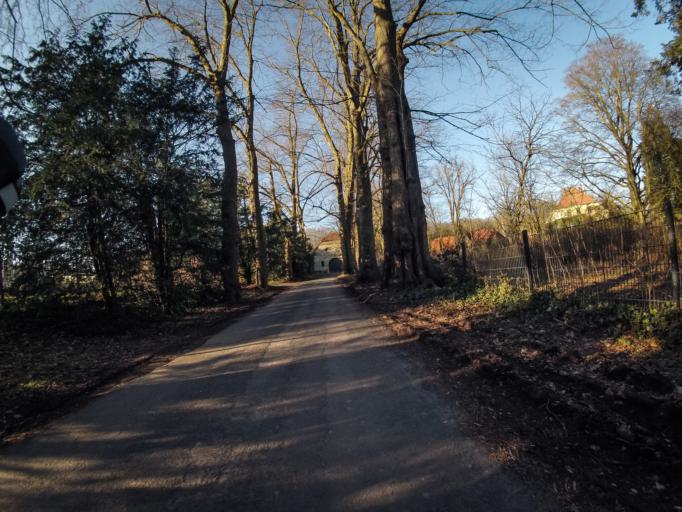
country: DE
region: Lower Saxony
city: Osnabrueck
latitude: 52.3085
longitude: 8.0309
